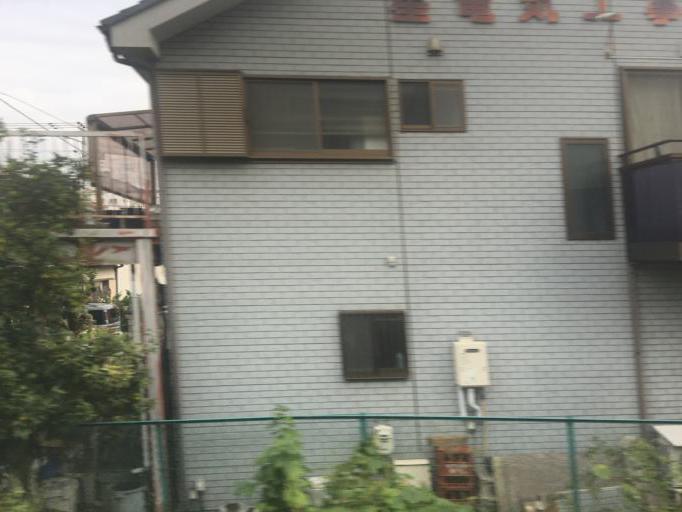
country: JP
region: Tokyo
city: Fussa
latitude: 35.7423
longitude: 139.3360
